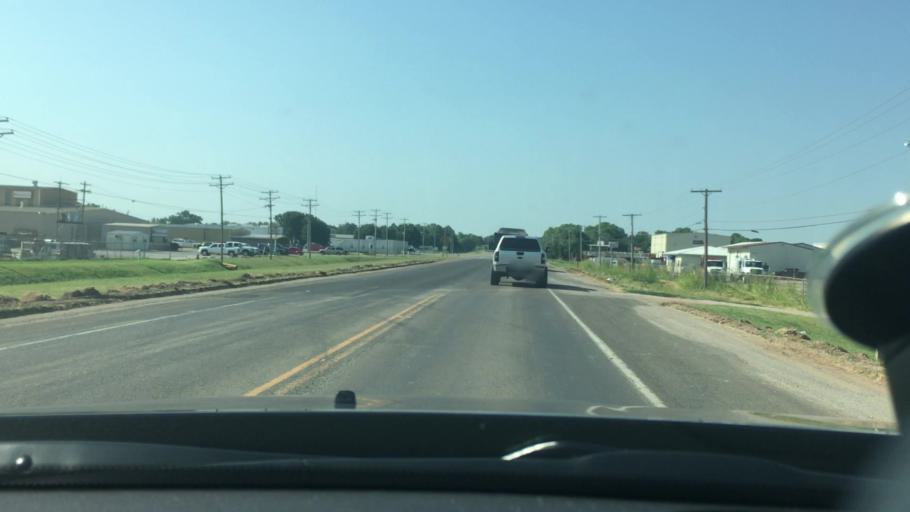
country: US
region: Oklahoma
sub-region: Garvin County
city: Lindsay
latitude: 34.8255
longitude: -97.5985
